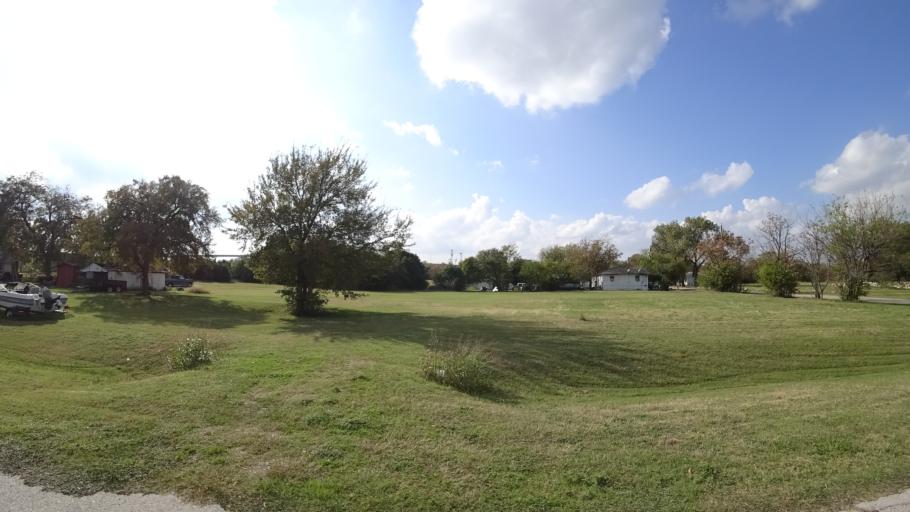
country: US
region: Texas
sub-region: Williamson County
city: Round Rock
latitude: 30.5024
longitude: -97.6777
